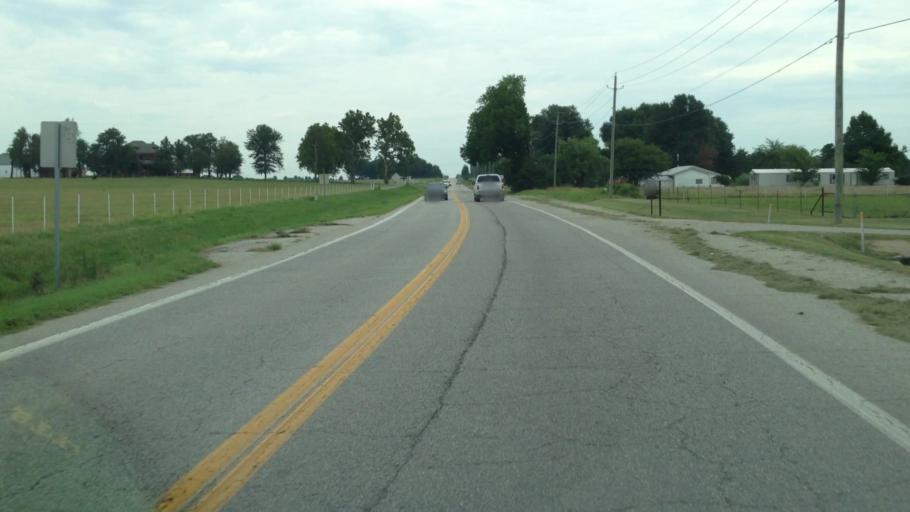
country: US
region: Oklahoma
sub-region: Craig County
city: Vinita
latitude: 36.6580
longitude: -95.1436
